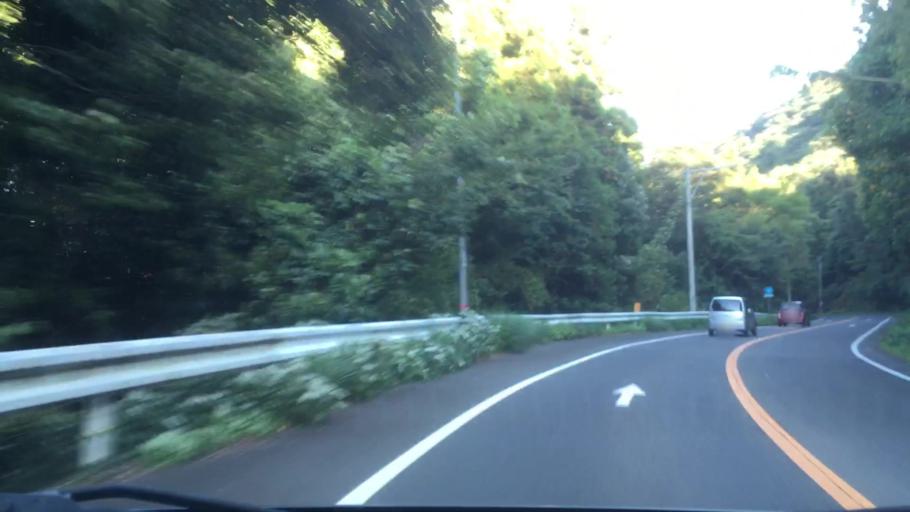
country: JP
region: Nagasaki
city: Sasebo
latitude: 33.0387
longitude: 129.6773
